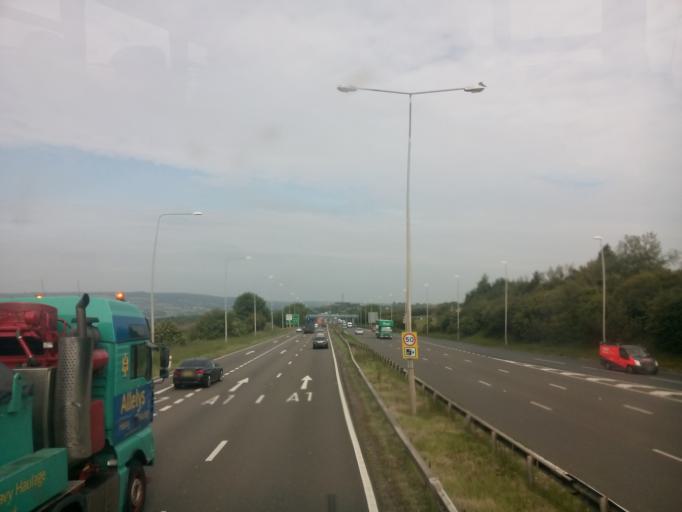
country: GB
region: England
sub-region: Gateshead
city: Lamesley
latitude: 54.9062
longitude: -1.5668
